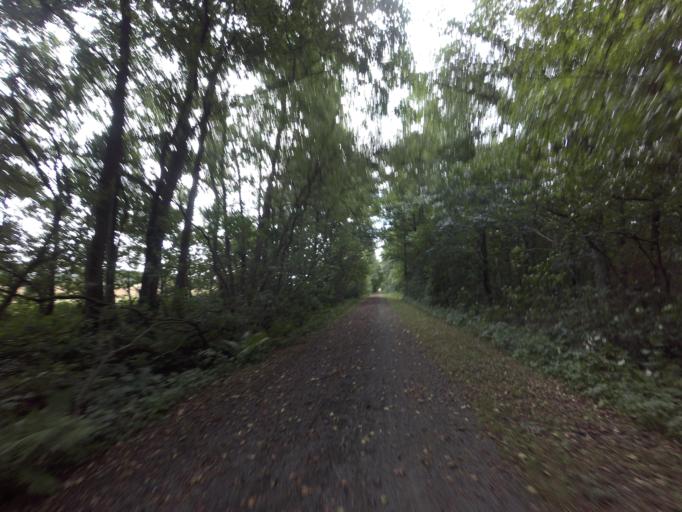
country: SE
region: Skane
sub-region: Helsingborg
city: Odakra
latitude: 56.1717
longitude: 12.7047
